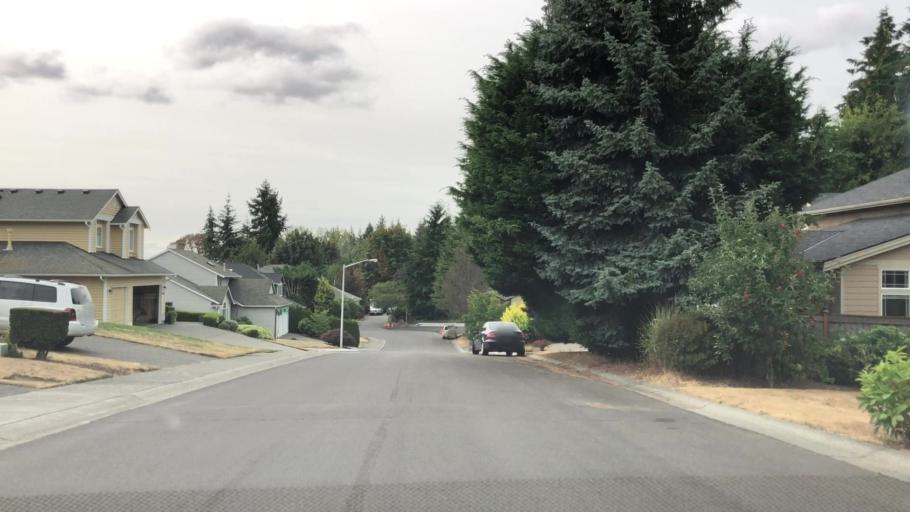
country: US
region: Washington
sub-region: King County
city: Inglewood-Finn Hill
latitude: 47.7135
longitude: -122.2333
